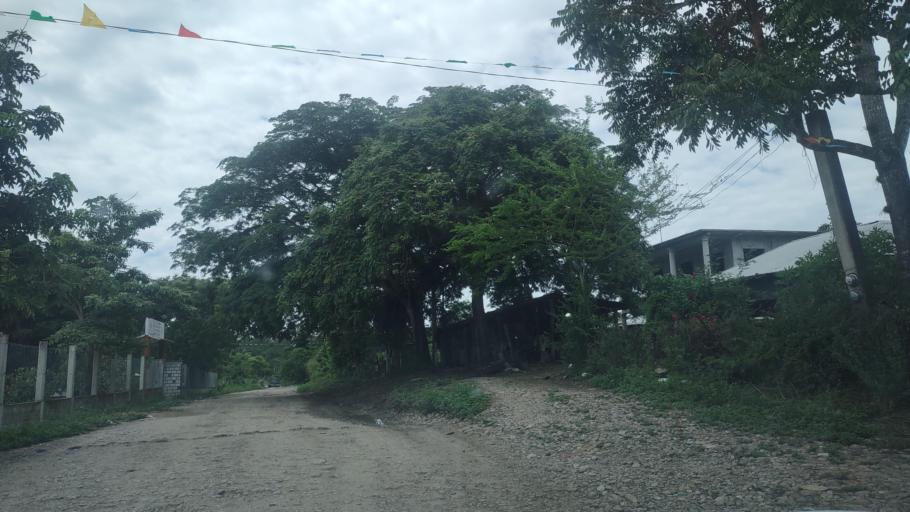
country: MX
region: Veracruz
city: Chicontepec de Tejada
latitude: 21.0485
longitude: -98.0019
